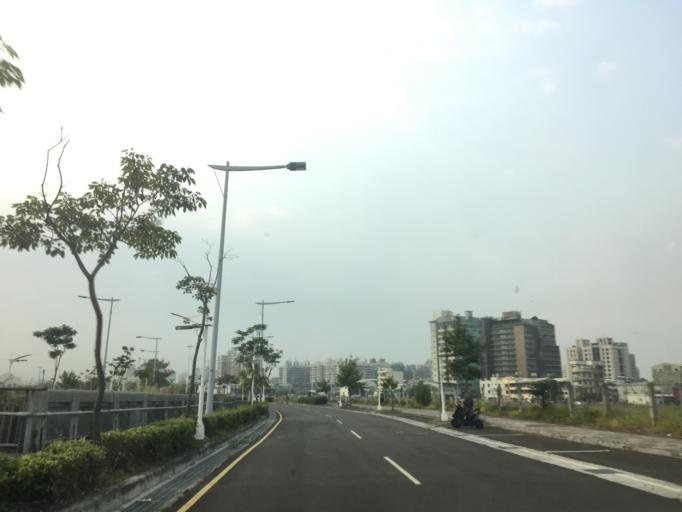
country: TW
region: Taiwan
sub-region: Taichung City
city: Taichung
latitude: 24.1944
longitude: 120.6683
